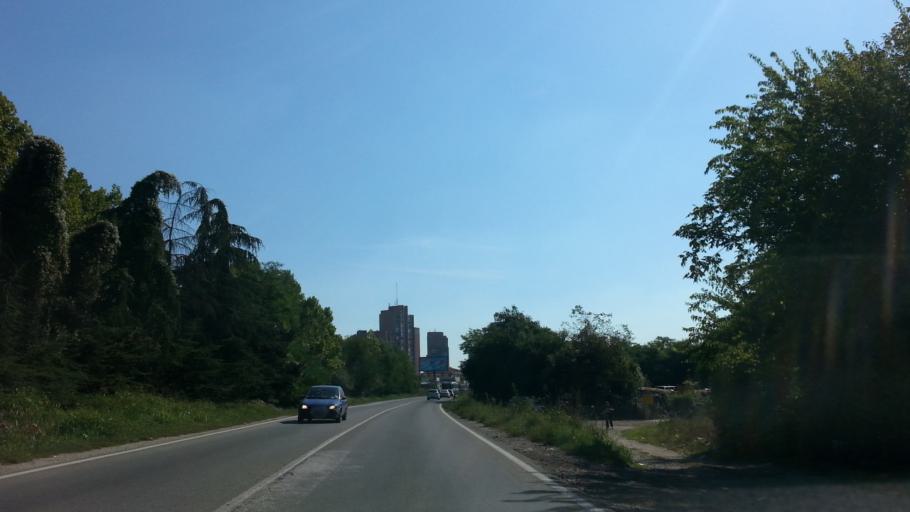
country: RS
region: Central Serbia
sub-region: Belgrade
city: Rakovica
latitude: 44.7383
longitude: 20.4170
